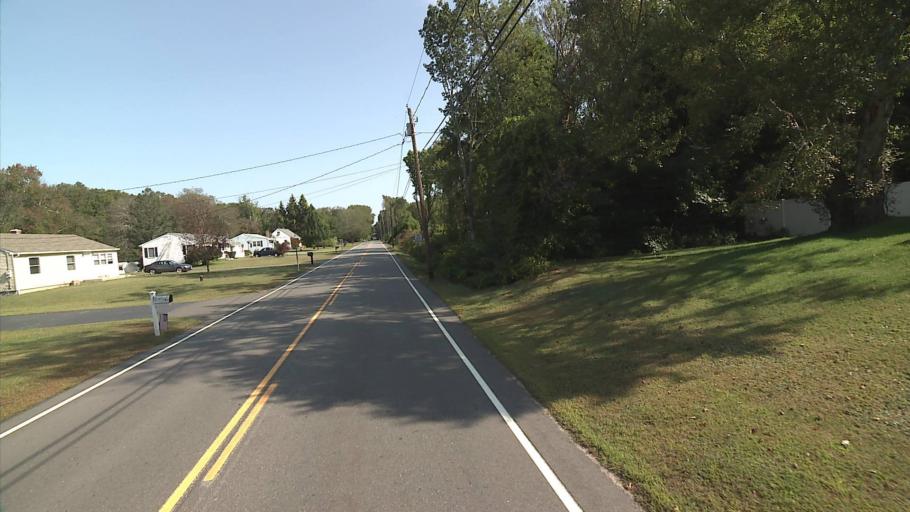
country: US
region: Connecticut
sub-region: New London County
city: Lisbon
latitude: 41.5841
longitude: -72.0248
